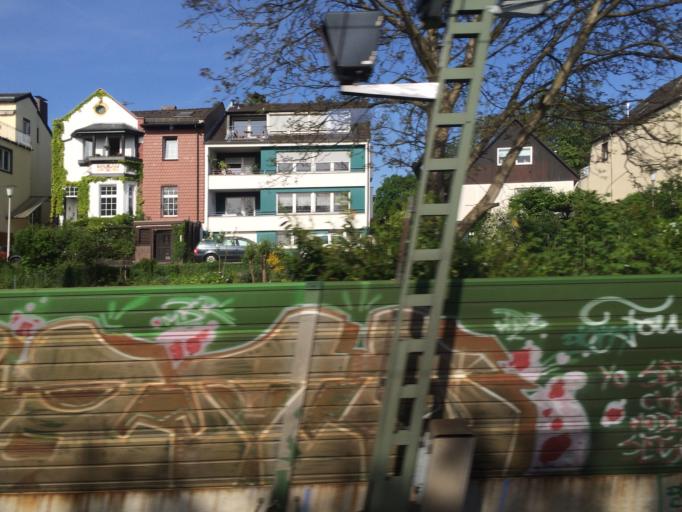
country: DE
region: North Rhine-Westphalia
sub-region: Regierungsbezirk Koln
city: Konigswinter
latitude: 50.7069
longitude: 7.1692
